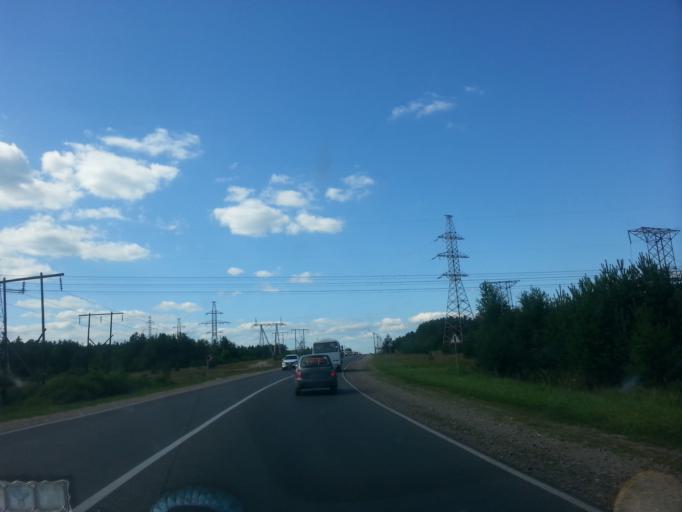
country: RU
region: Nizjnij Novgorod
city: Lukino
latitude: 56.3895
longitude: 43.6982
